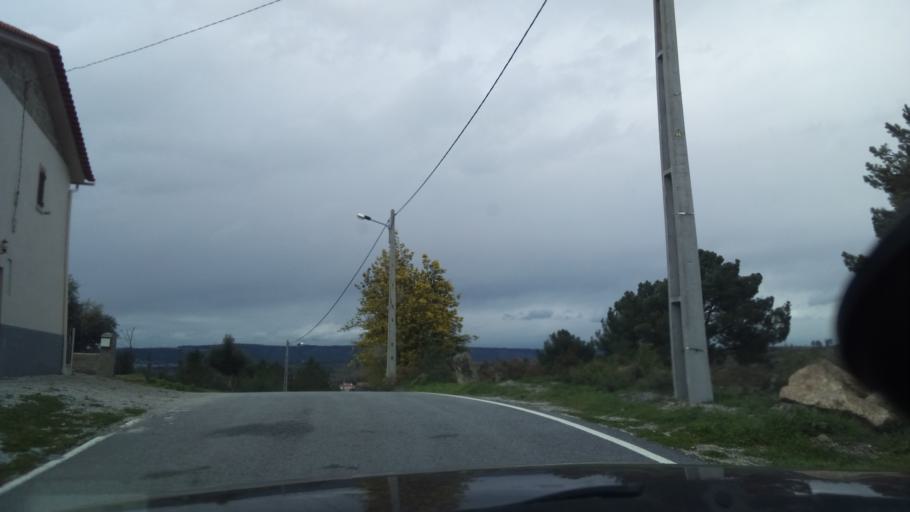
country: PT
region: Guarda
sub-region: Fornos de Algodres
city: Fornos de Algodres
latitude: 40.5765
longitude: -7.4695
